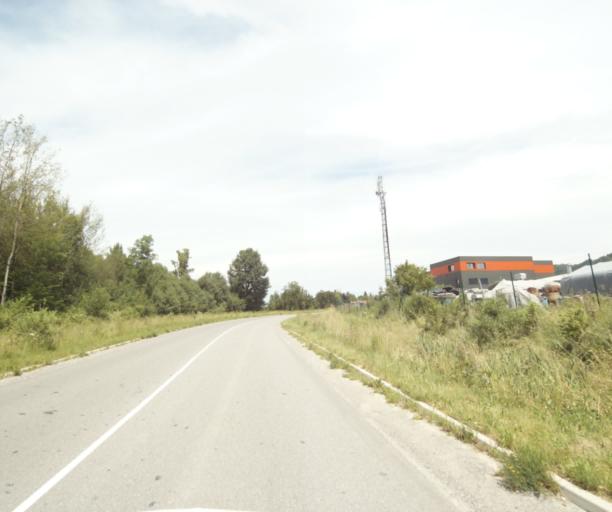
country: FR
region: Rhone-Alpes
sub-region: Departement de la Haute-Savoie
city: Margencel
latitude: 46.3252
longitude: 6.4357
